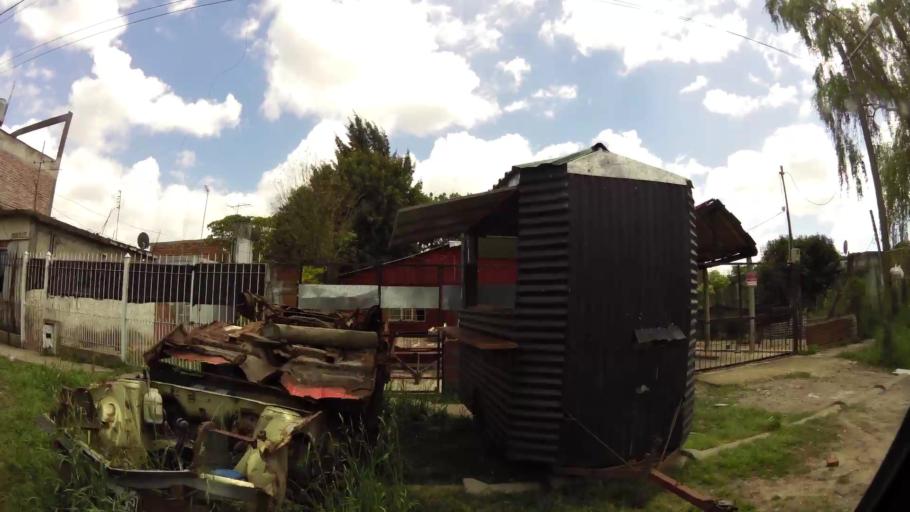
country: AR
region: Buenos Aires
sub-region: Partido de Quilmes
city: Quilmes
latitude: -34.8232
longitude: -58.2466
